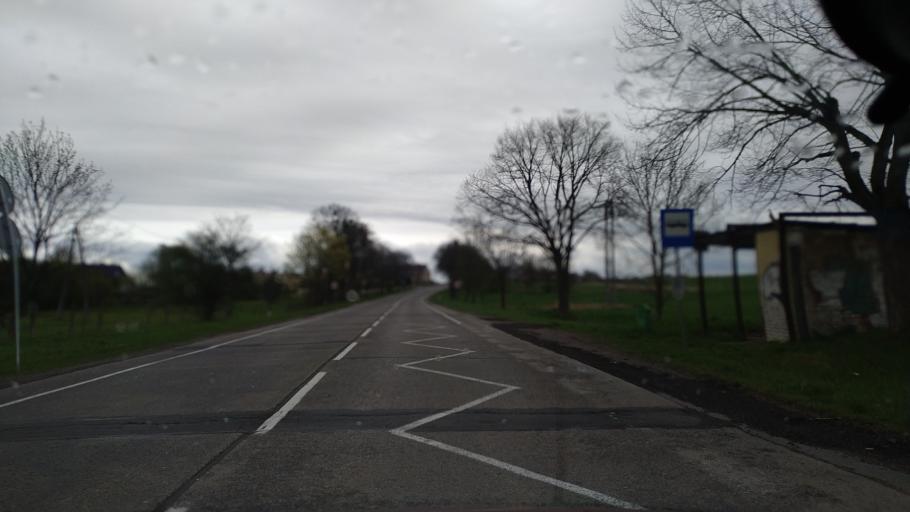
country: PL
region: Pomeranian Voivodeship
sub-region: Powiat starogardzki
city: Zblewo
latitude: 53.9322
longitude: 18.3774
